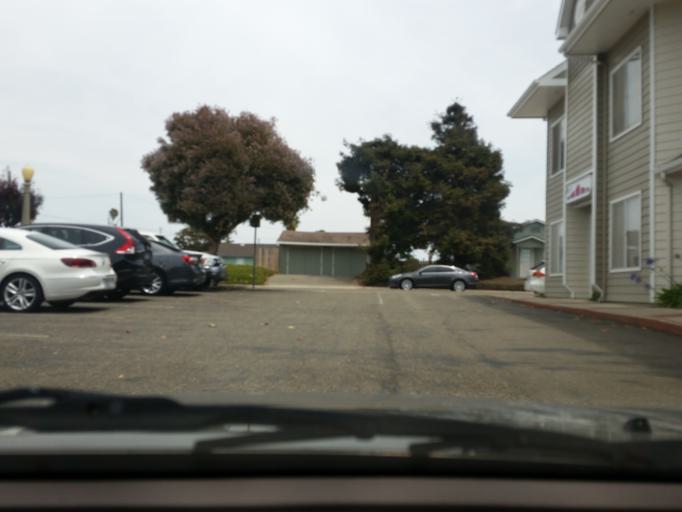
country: US
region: California
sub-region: San Luis Obispo County
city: Grover Beach
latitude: 35.1222
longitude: -120.6193
